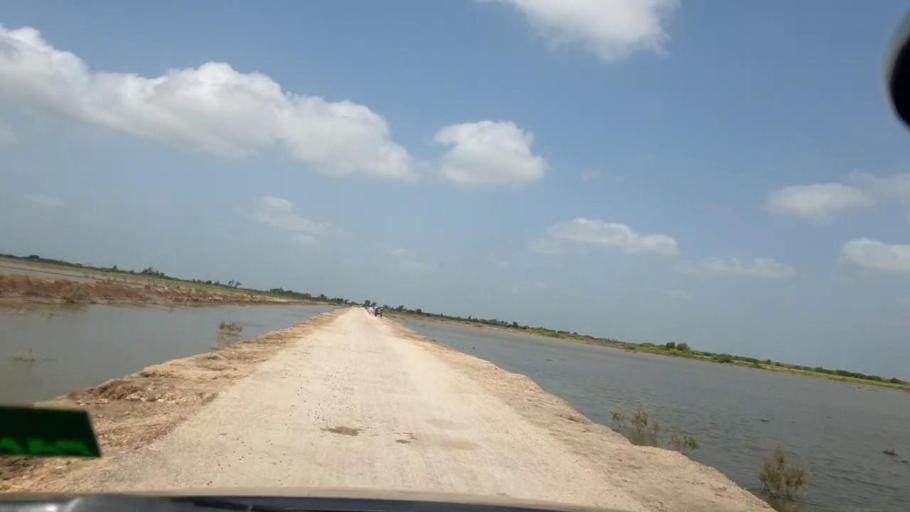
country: PK
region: Sindh
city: Kadhan
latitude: 24.5962
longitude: 69.1295
